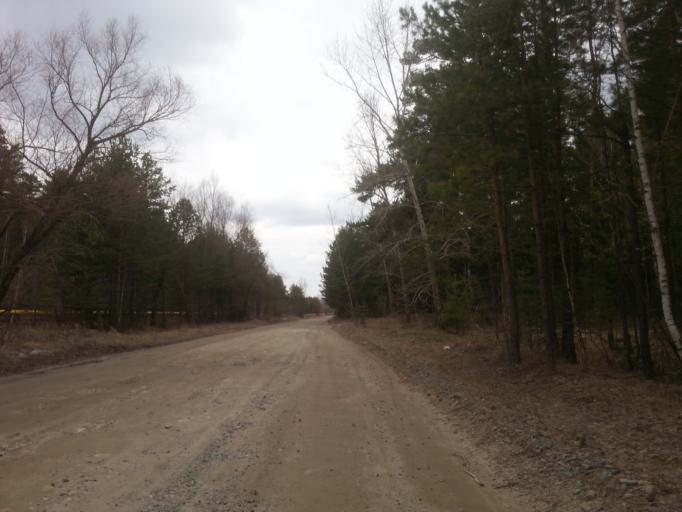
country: RU
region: Altai Krai
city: Yuzhnyy
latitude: 53.2815
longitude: 83.7340
